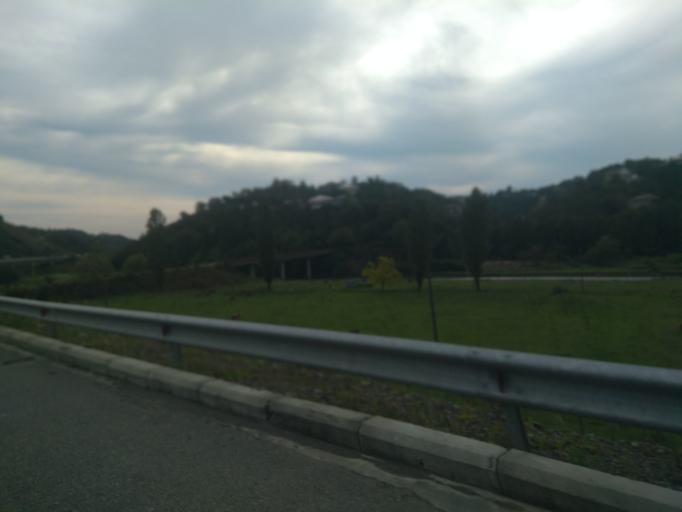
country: GE
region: Ajaria
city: Kobuleti
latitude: 41.7758
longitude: 41.7865
